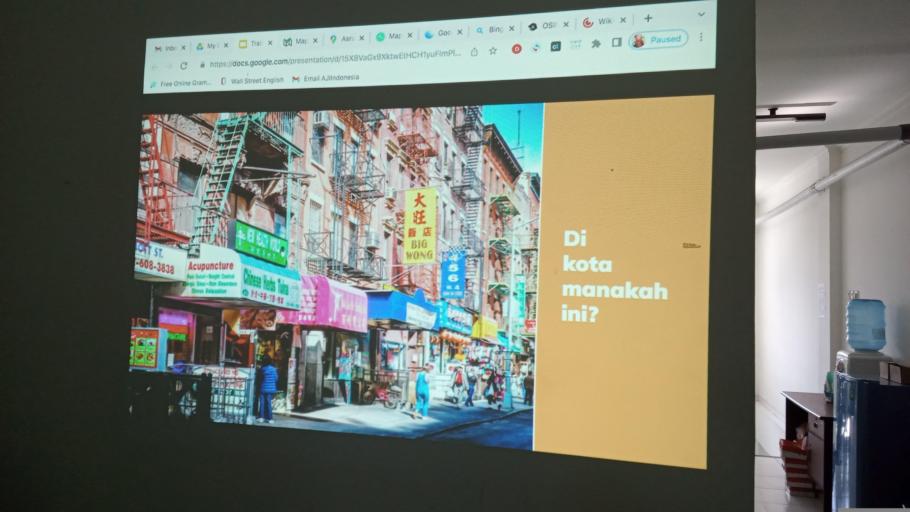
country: ID
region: Papua
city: Abepura
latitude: -2.5973
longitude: 140.6395
